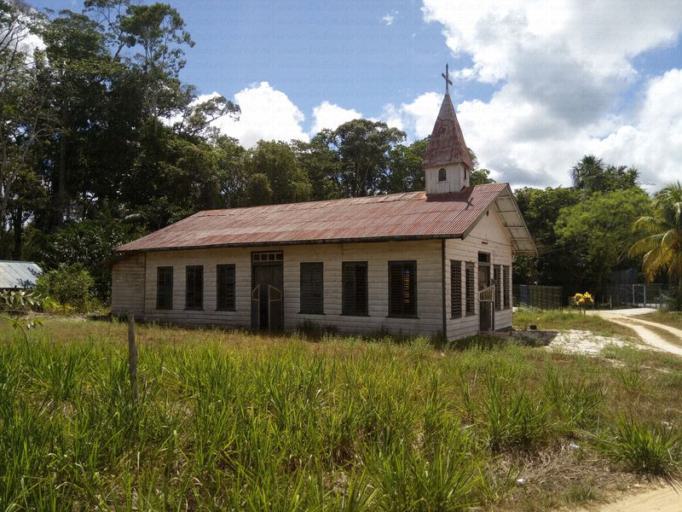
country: SR
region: Para
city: Onverwacht
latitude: 5.3985
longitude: -55.1845
